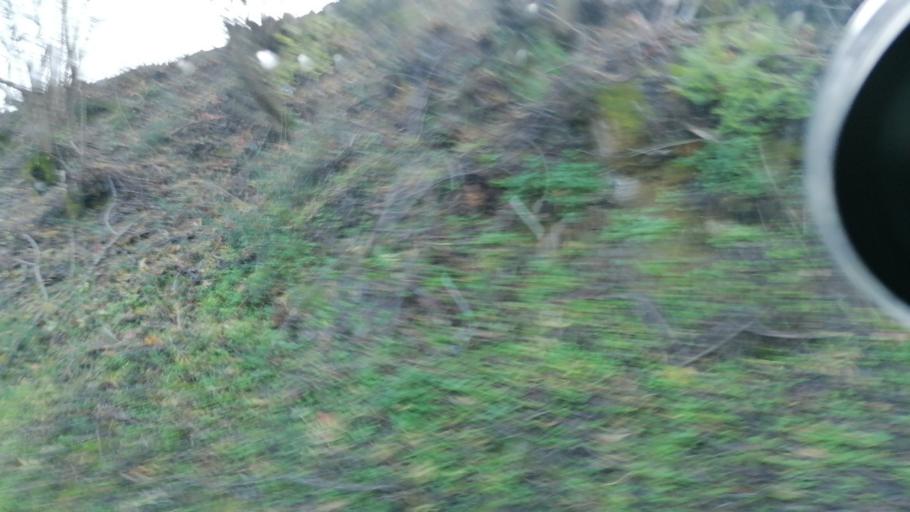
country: PT
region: Vila Real
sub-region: Peso da Regua
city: Peso da Regua
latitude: 41.1478
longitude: -7.7792
